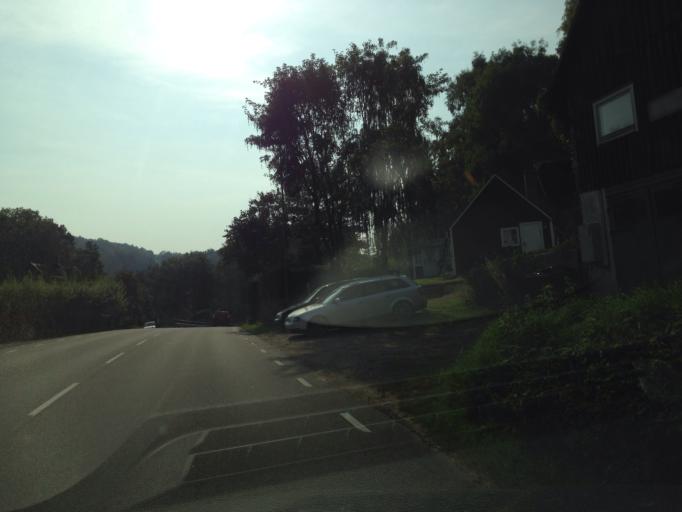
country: SE
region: Skane
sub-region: Bastads Kommun
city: Bastad
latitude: 56.4149
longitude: 12.8479
